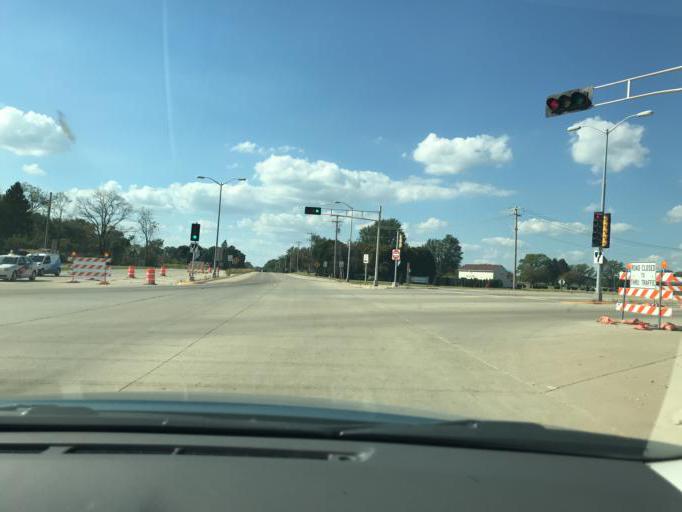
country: US
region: Wisconsin
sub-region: Walworth County
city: Williams Bay
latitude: 42.6001
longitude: -88.5406
